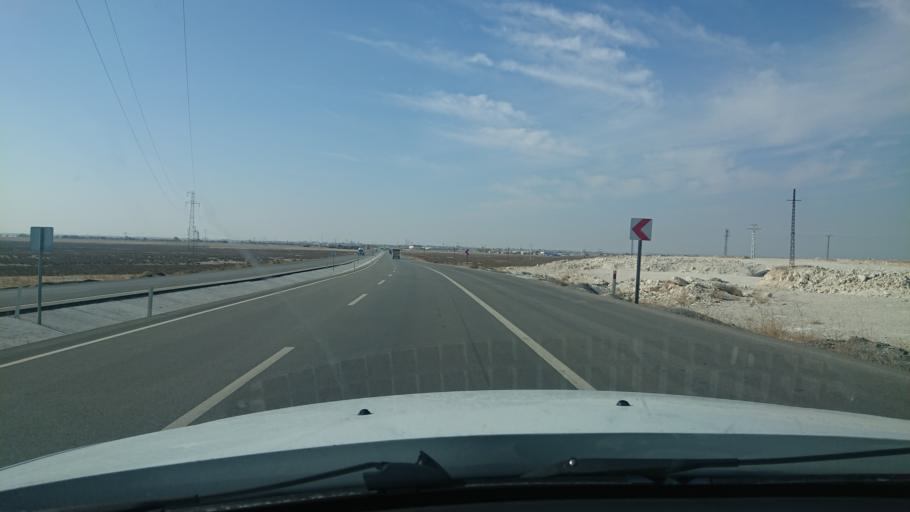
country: TR
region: Aksaray
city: Sultanhani
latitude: 38.2534
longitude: 33.4954
